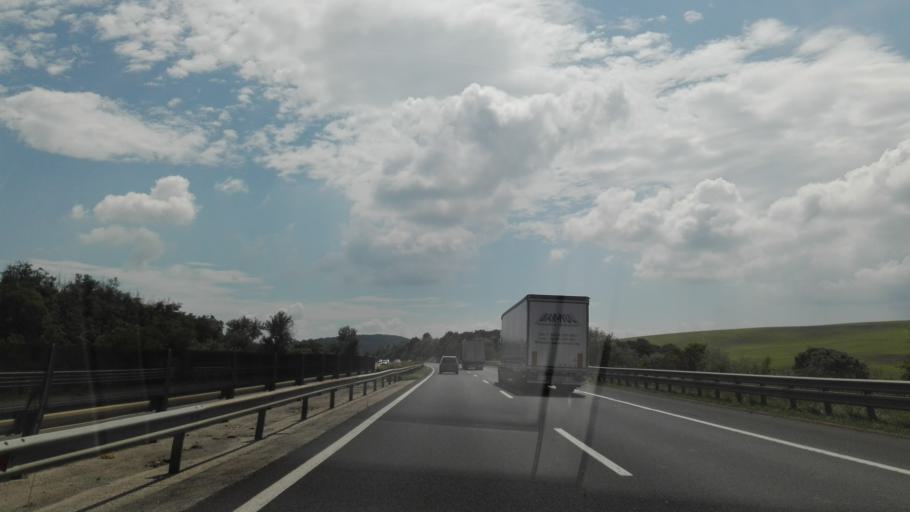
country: HU
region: Fejer
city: Szarliget
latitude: 47.5650
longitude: 18.4788
